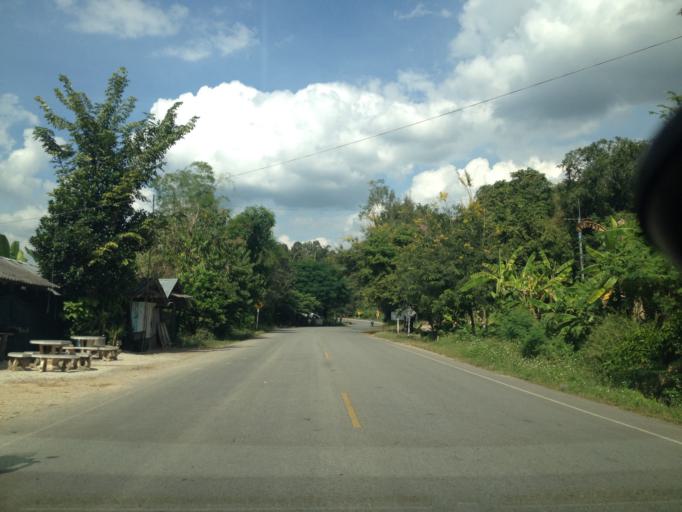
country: TH
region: Chiang Mai
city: Hang Dong
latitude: 18.7668
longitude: 98.8702
